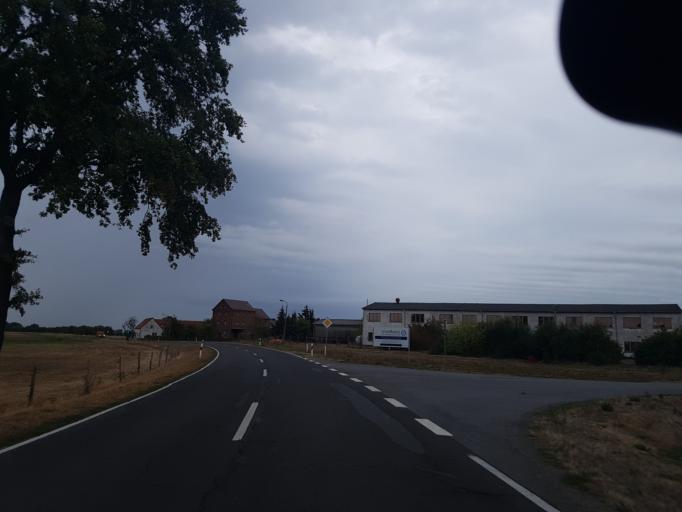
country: DE
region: Saxony-Anhalt
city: Jessen
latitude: 51.7563
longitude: 12.8902
